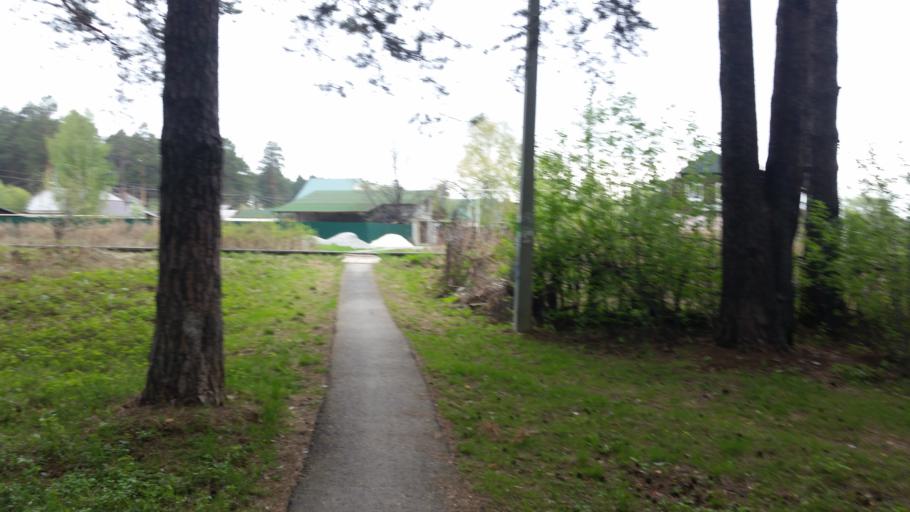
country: RU
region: Sverdlovsk
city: Beryozovsky
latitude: 56.9032
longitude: 60.7646
